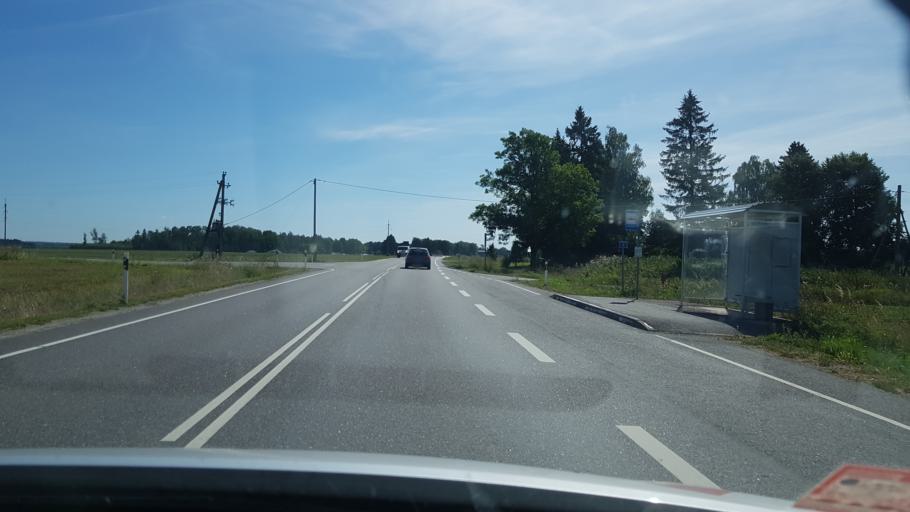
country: EE
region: Tartu
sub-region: Tartu linn
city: Tartu
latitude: 58.4189
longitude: 26.8730
